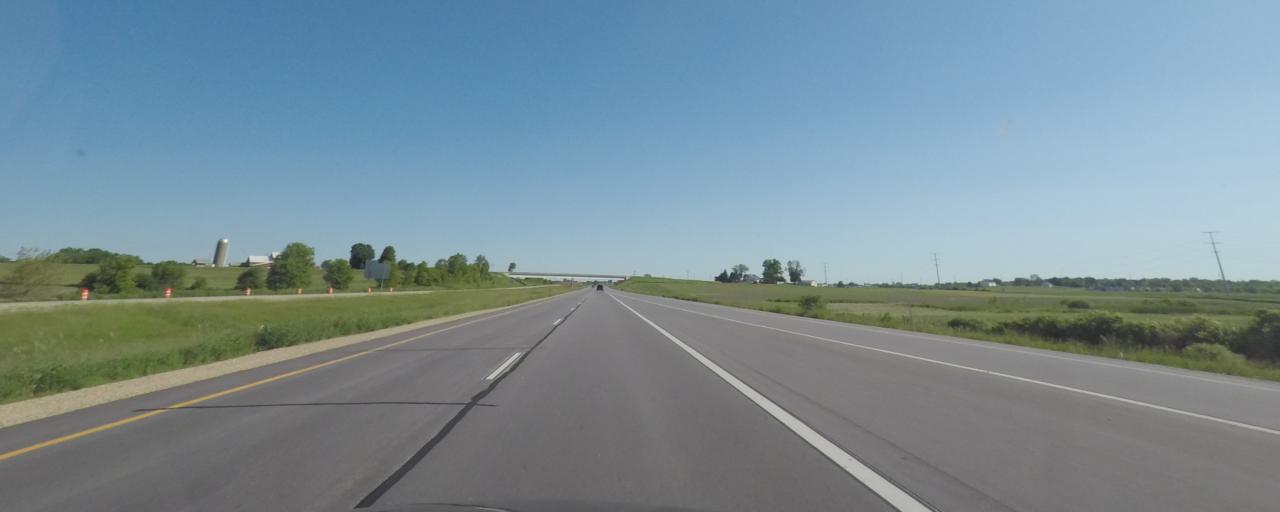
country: US
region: Wisconsin
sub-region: Columbia County
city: Columbus
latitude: 43.3218
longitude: -89.0450
